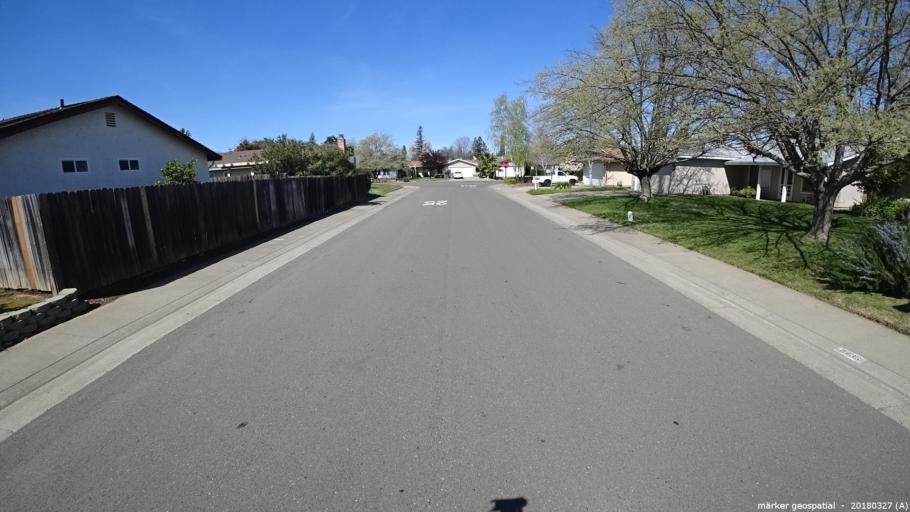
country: US
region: California
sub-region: Sacramento County
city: La Riviera
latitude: 38.5540
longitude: -121.3482
